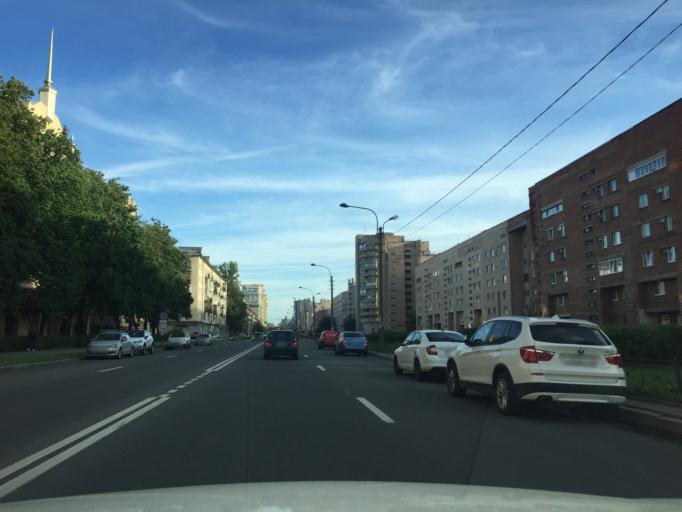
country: RU
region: St.-Petersburg
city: Kupchino
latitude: 59.8639
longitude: 30.3140
